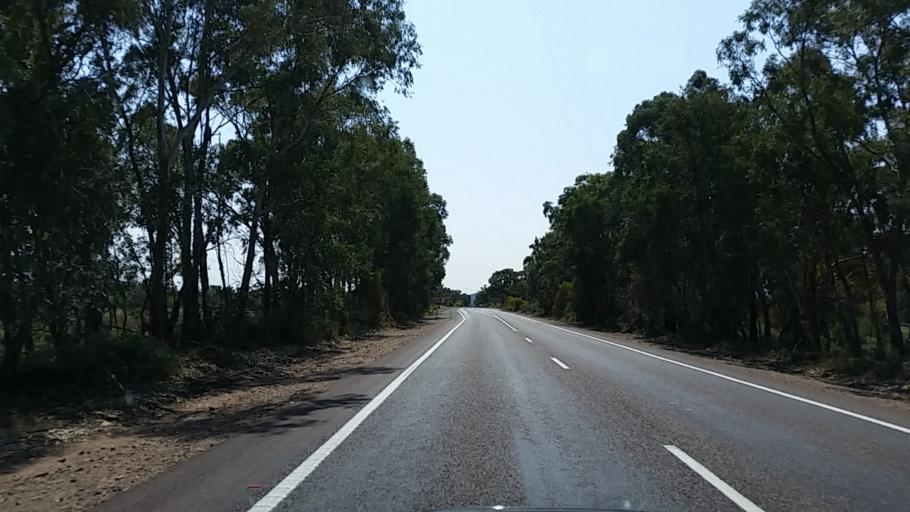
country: AU
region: South Australia
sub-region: Port Pirie City and Dists
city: Port Pirie
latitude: -32.8538
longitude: 137.9821
